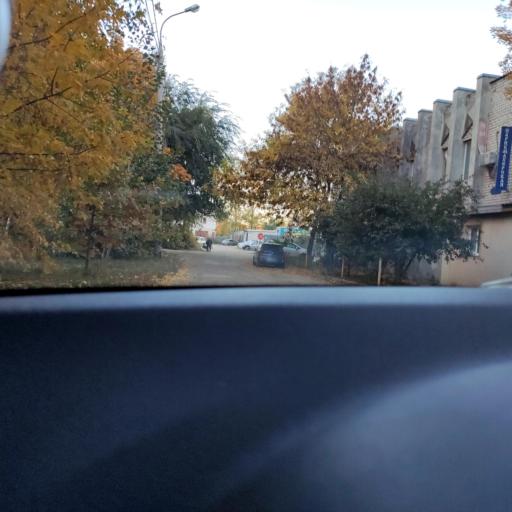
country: RU
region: Samara
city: Samara
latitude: 53.2107
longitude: 50.2555
